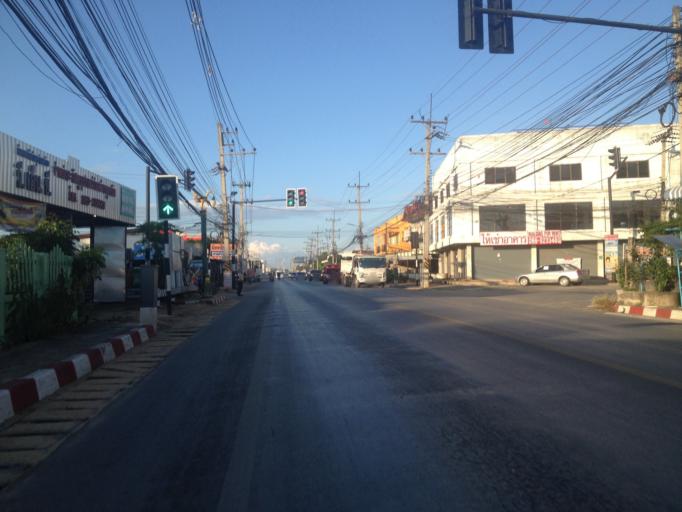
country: TH
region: Chiang Mai
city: San Pa Tong
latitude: 18.6316
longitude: 98.8974
